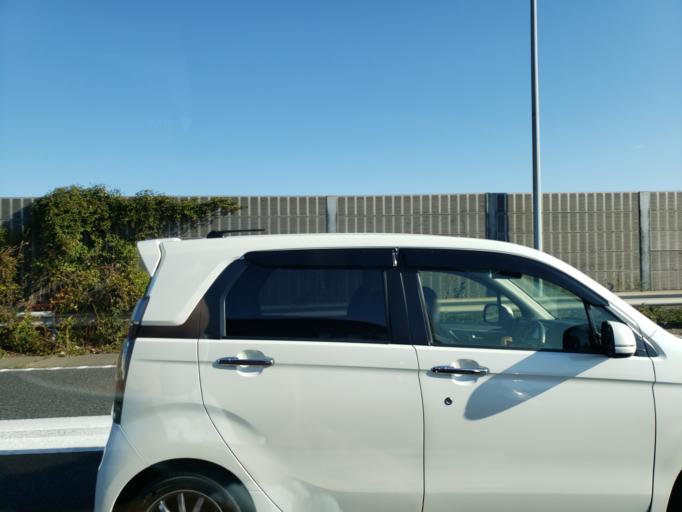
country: JP
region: Hyogo
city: Akashi
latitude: 34.6860
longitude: 134.9782
